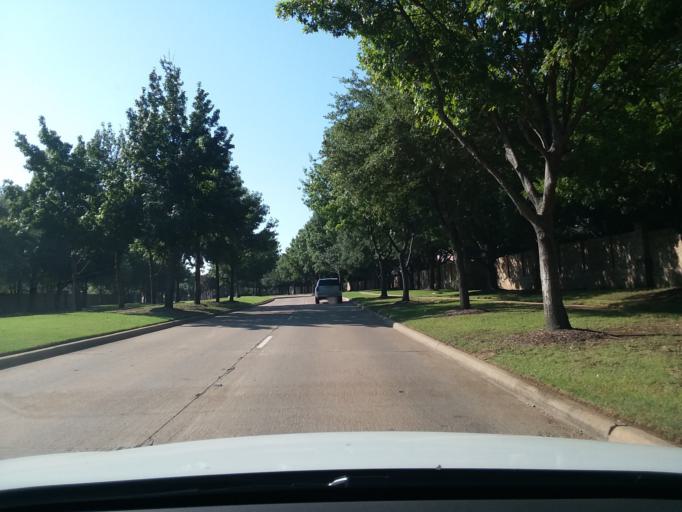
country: US
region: Texas
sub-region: Denton County
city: Flower Mound
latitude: 33.0235
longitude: -97.0836
